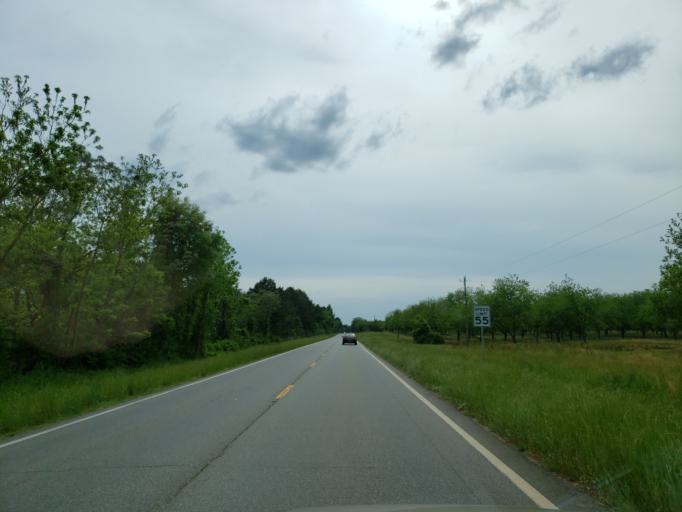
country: US
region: Georgia
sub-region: Macon County
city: Marshallville
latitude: 32.4218
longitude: -83.8402
